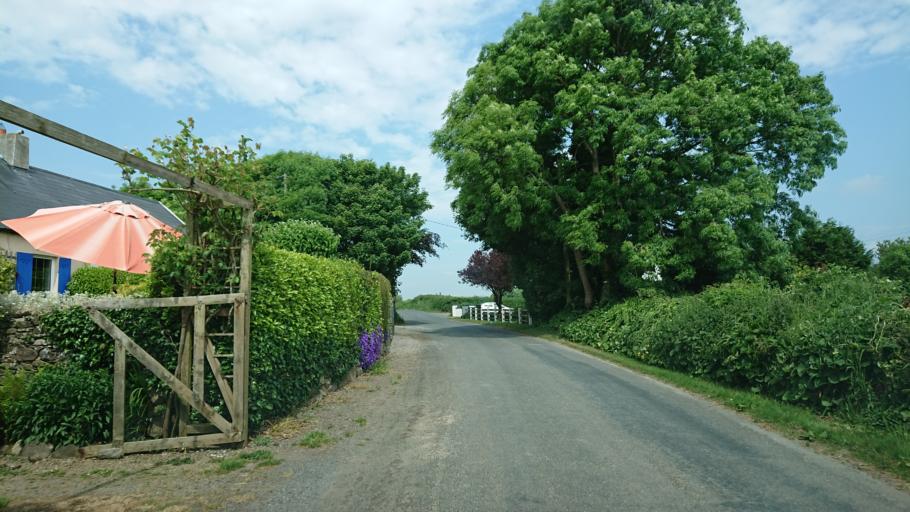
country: IE
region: Munster
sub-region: Waterford
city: Dunmore East
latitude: 52.2159
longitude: -6.9976
